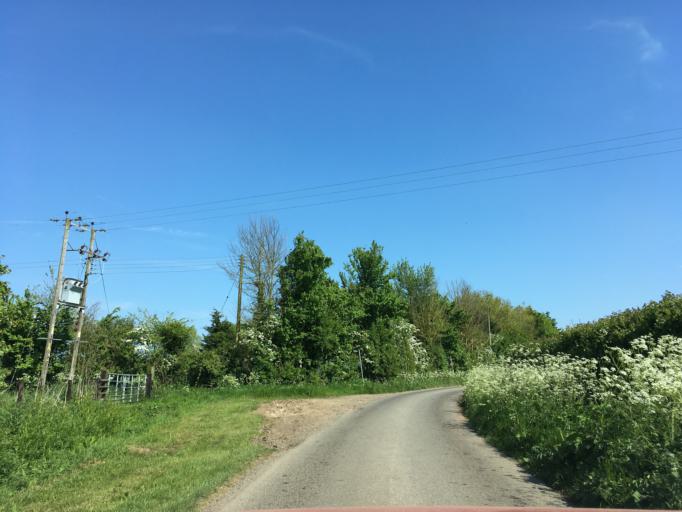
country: GB
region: England
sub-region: Gloucestershire
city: Dursley
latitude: 51.7207
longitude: -2.3856
